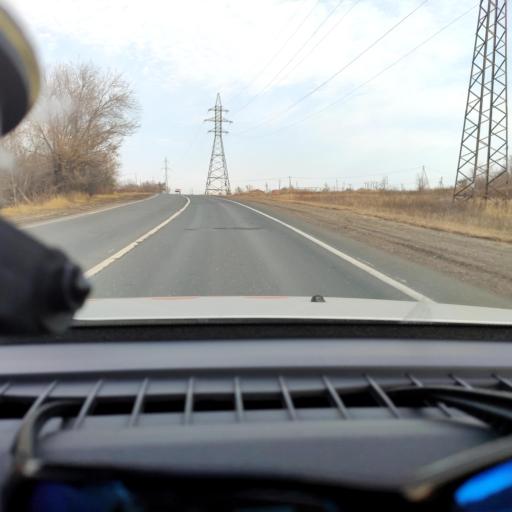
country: RU
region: Samara
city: Chapayevsk
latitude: 52.9904
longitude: 49.7669
